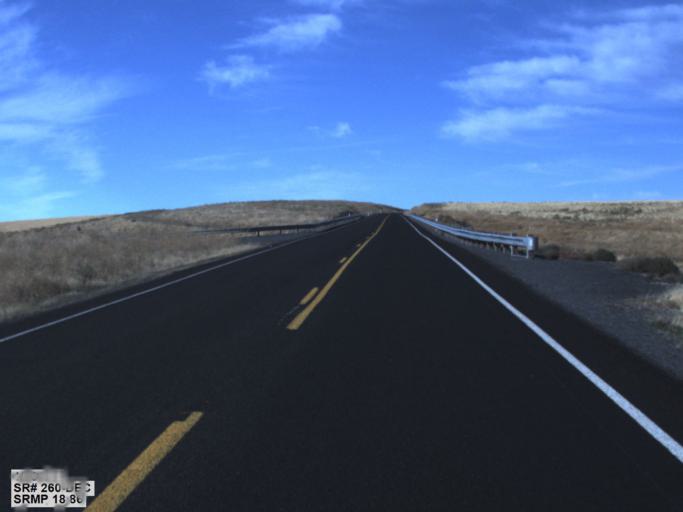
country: US
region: Washington
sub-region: Franklin County
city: Connell
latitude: 46.6213
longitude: -118.6615
